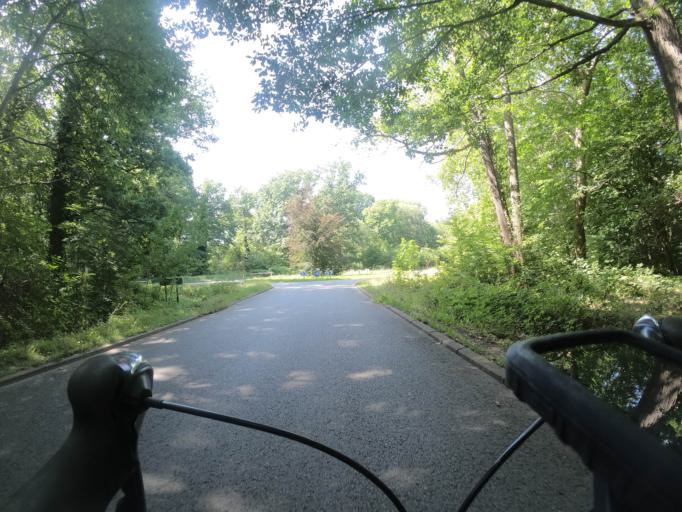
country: FR
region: Ile-de-France
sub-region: Departement des Yvelines
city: Velizy-Villacoublay
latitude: 48.7933
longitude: 2.1966
